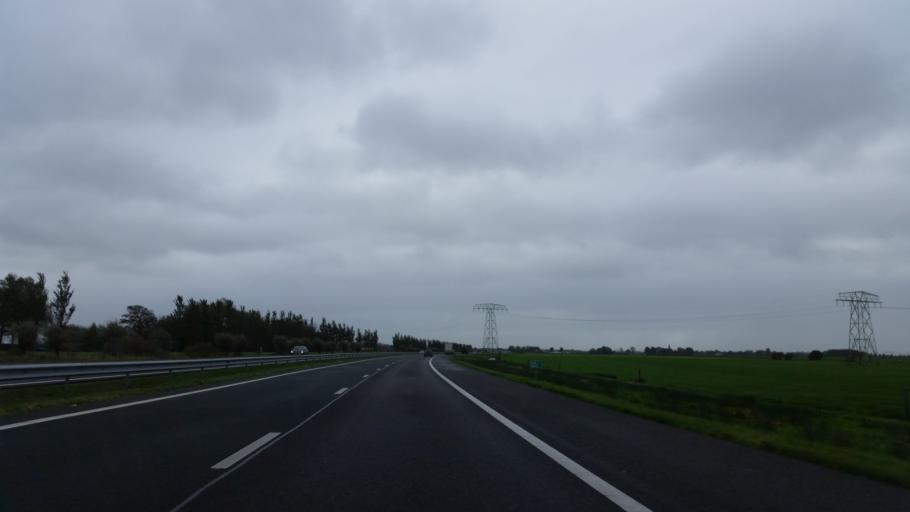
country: NL
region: Friesland
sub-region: Gemeente Boarnsterhim
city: Nes
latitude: 53.0207
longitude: 5.8668
